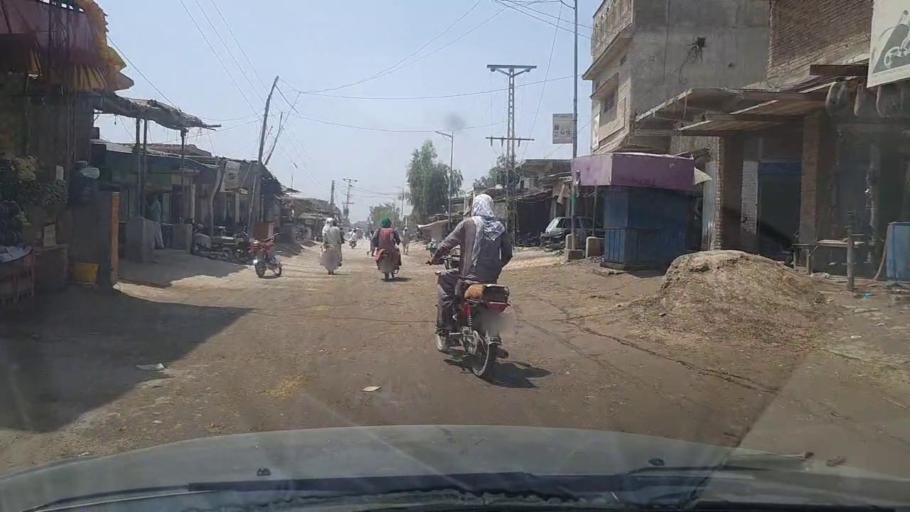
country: PK
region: Sindh
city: Bhiria
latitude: 26.8849
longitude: 68.2873
